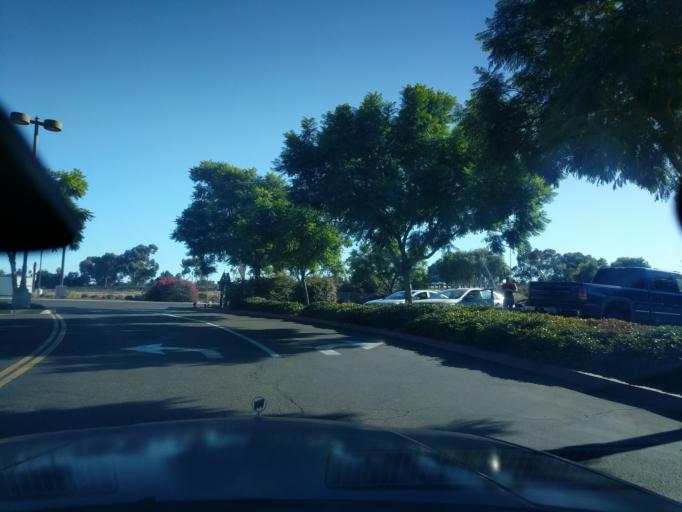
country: US
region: California
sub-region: Santa Barbara County
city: Goleta
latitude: 34.4415
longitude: -119.8321
